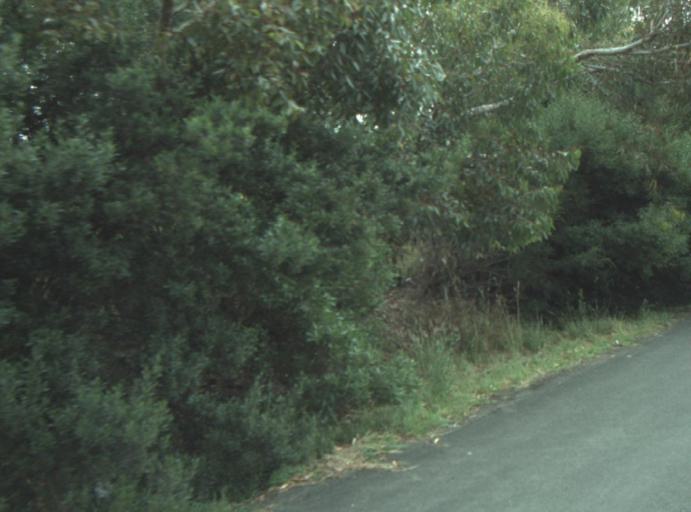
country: AU
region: Victoria
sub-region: Greater Geelong
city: Clifton Springs
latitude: -38.1828
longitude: 144.5283
